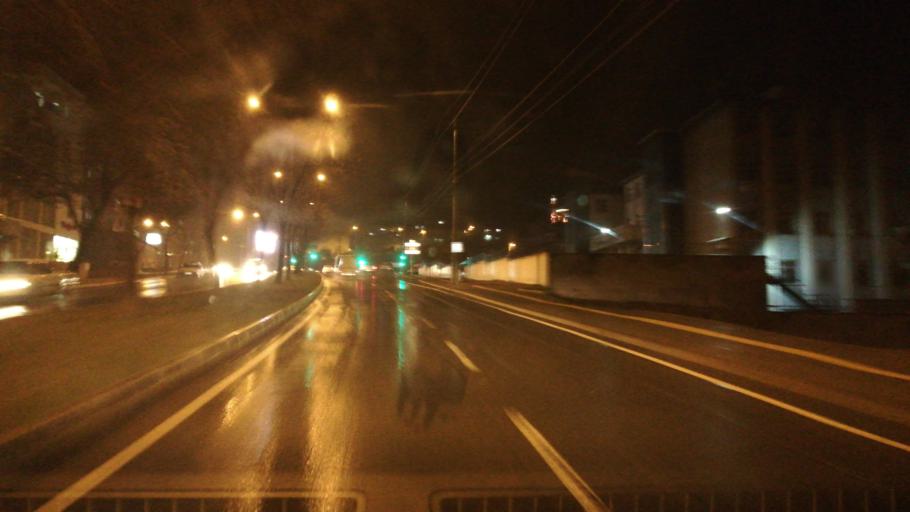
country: TR
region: Kahramanmaras
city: Kahramanmaras
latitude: 37.5855
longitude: 36.9458
